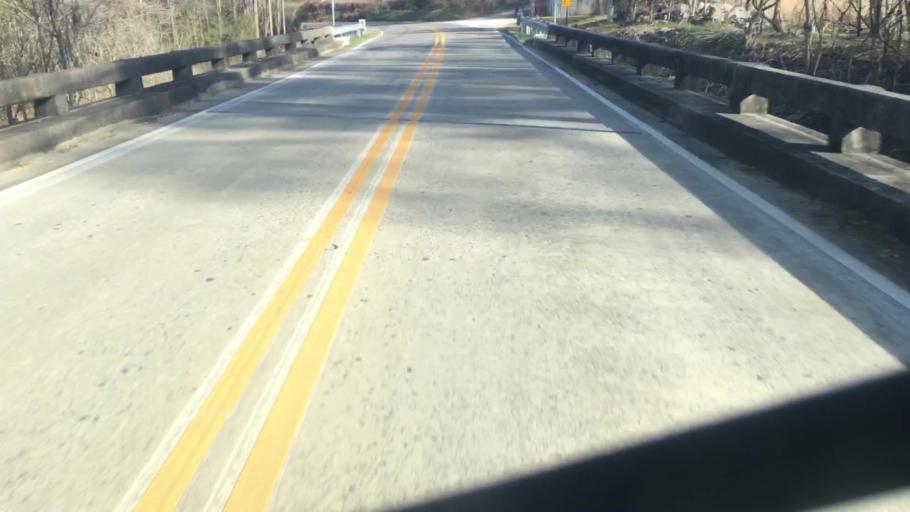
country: US
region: Alabama
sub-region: Jefferson County
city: Cahaba Heights
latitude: 33.4511
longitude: -86.7148
